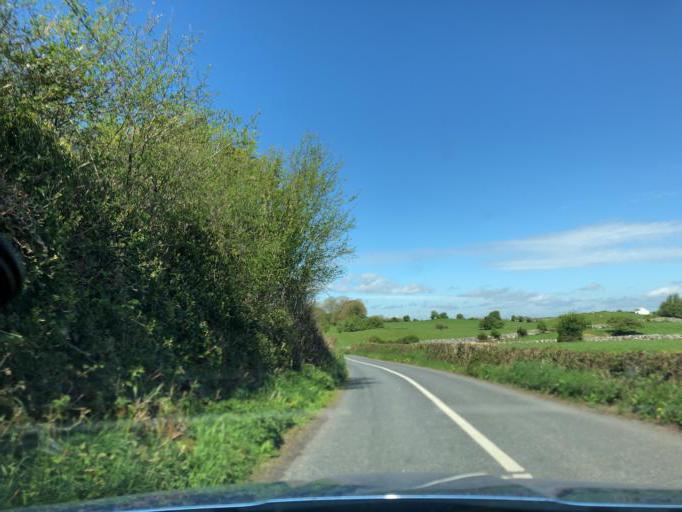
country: IE
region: Connaught
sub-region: County Galway
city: Loughrea
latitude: 53.1612
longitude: -8.3986
